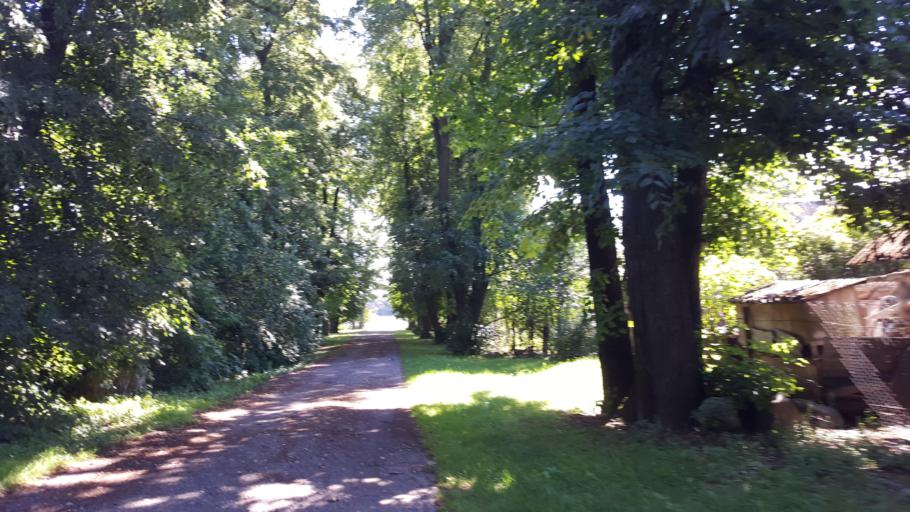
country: BY
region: Brest
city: Kamyanyets
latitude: 52.3845
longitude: 23.6577
